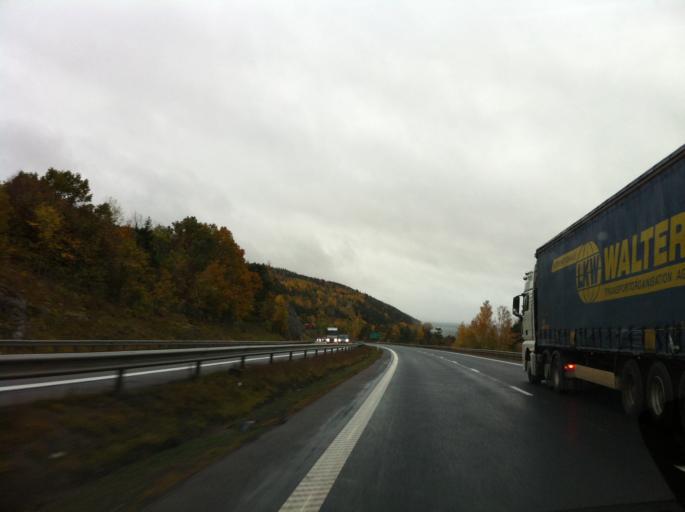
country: SE
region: Joenkoeping
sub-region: Jonkopings Kommun
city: Kaxholmen
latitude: 57.9223
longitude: 14.3141
